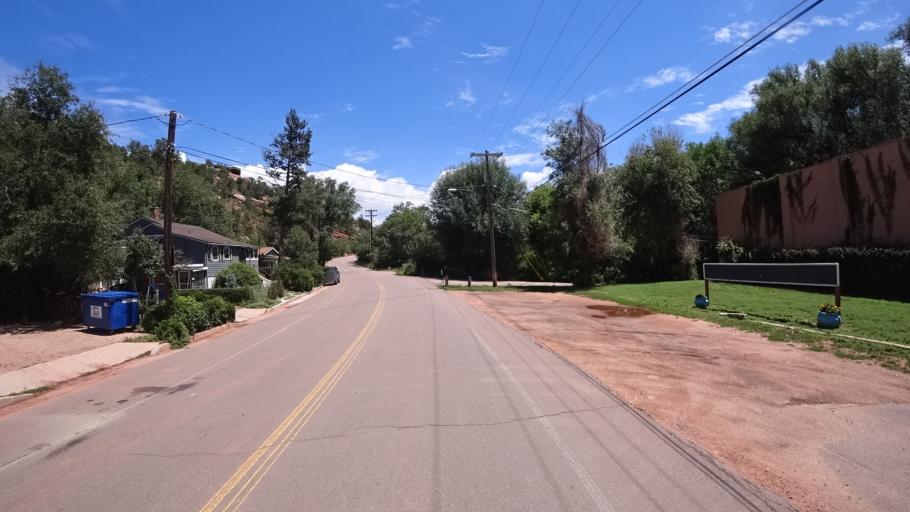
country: US
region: Colorado
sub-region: El Paso County
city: Manitou Springs
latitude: 38.8582
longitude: -104.9067
